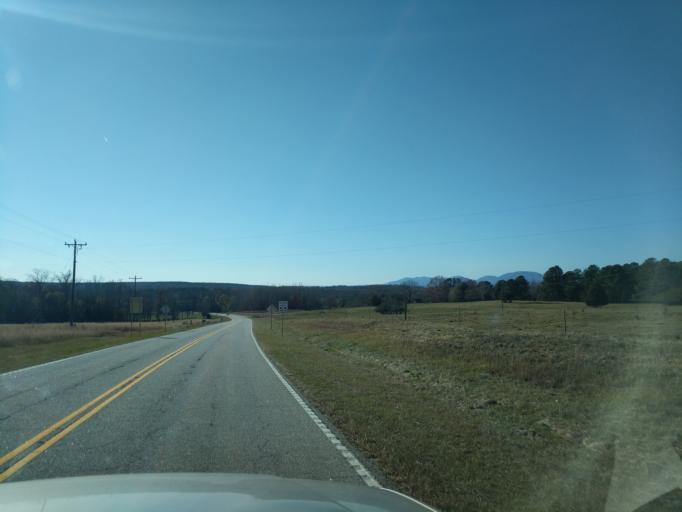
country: US
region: South Carolina
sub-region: Spartanburg County
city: Landrum
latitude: 35.1364
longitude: -82.1078
